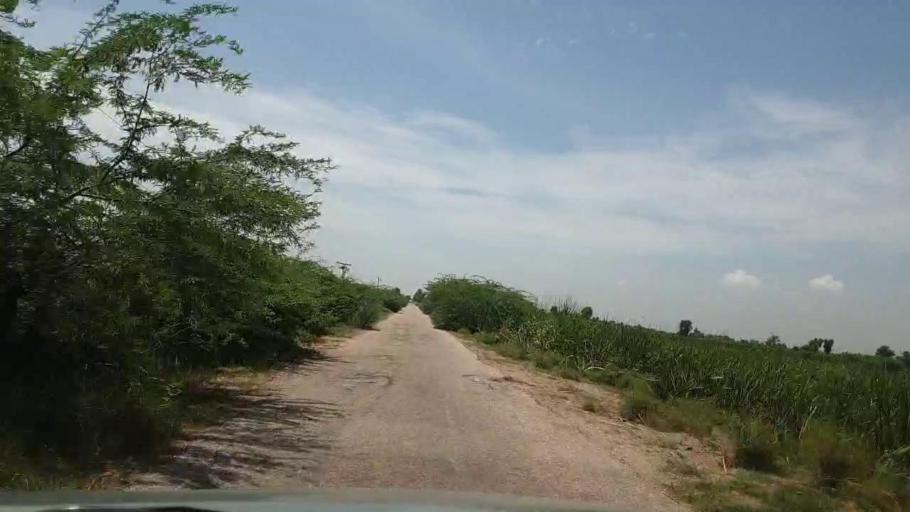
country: PK
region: Sindh
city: Bozdar
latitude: 27.0593
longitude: 68.9819
